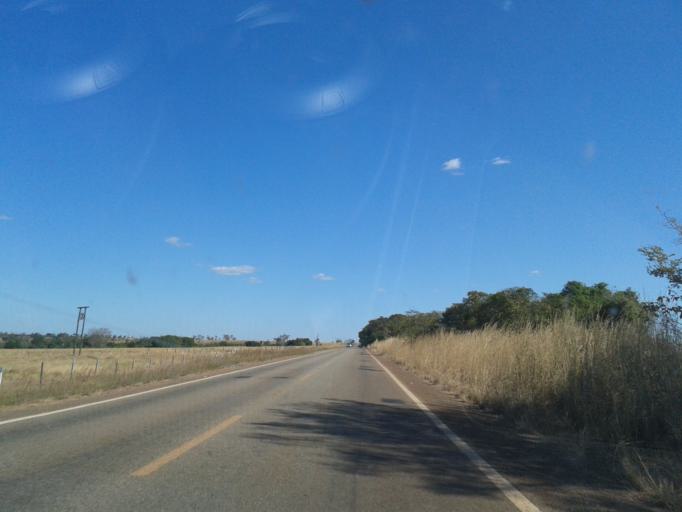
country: BR
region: Goias
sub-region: Mozarlandia
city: Mozarlandia
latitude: -14.3711
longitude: -50.4307
